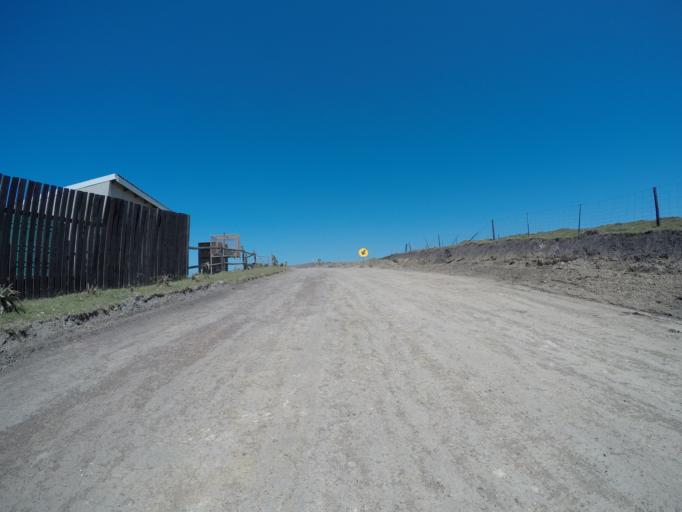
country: ZA
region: Eastern Cape
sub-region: OR Tambo District Municipality
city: Libode
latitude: -32.0370
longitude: 29.1089
